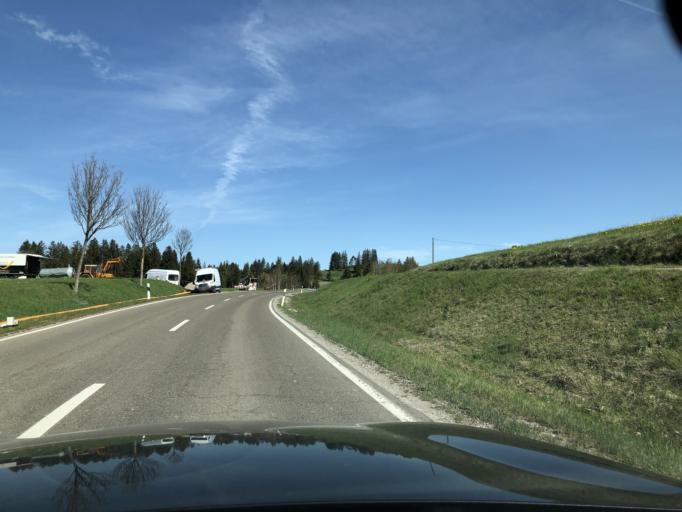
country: DE
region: Bavaria
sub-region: Swabia
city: Eisenberg
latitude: 47.6239
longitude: 10.6065
